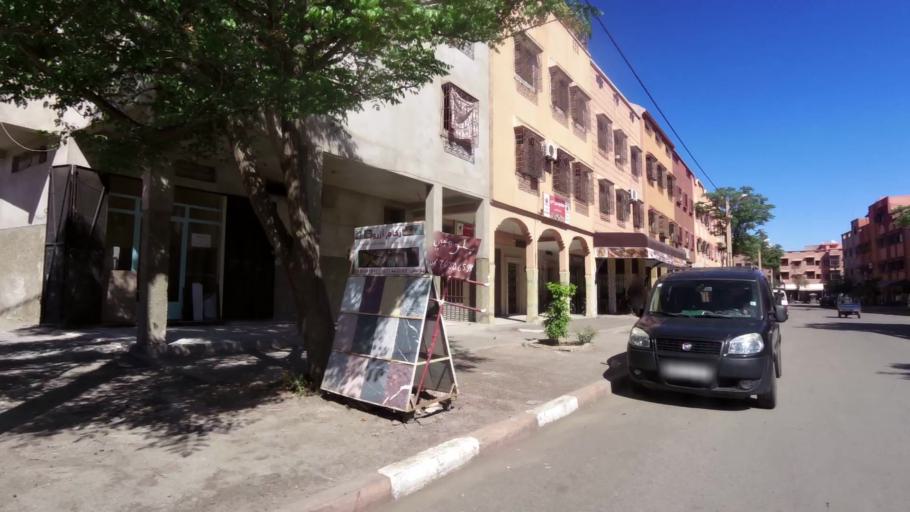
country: MA
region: Marrakech-Tensift-Al Haouz
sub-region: Marrakech
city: Marrakesh
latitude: 31.5951
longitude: -8.0467
